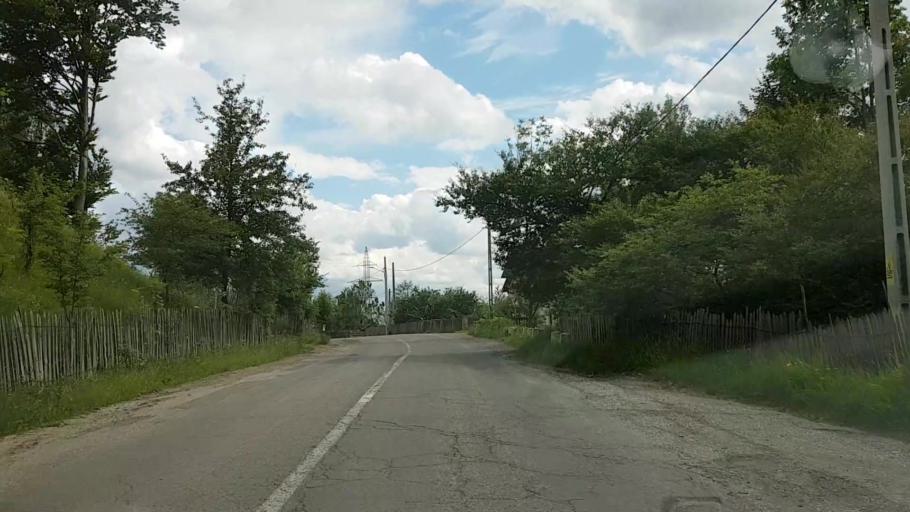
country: RO
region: Neamt
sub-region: Comuna Bicaz
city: Dodeni
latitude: 46.9880
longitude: 26.1018
